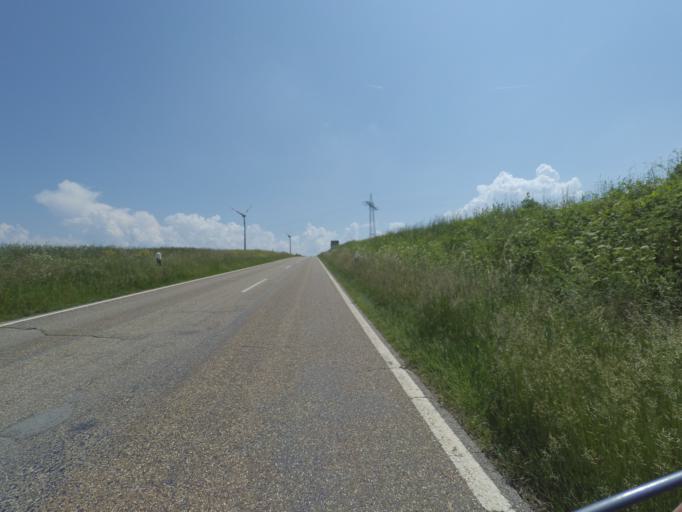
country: DE
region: Rheinland-Pfalz
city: Hambuch
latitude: 50.2388
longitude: 7.1787
